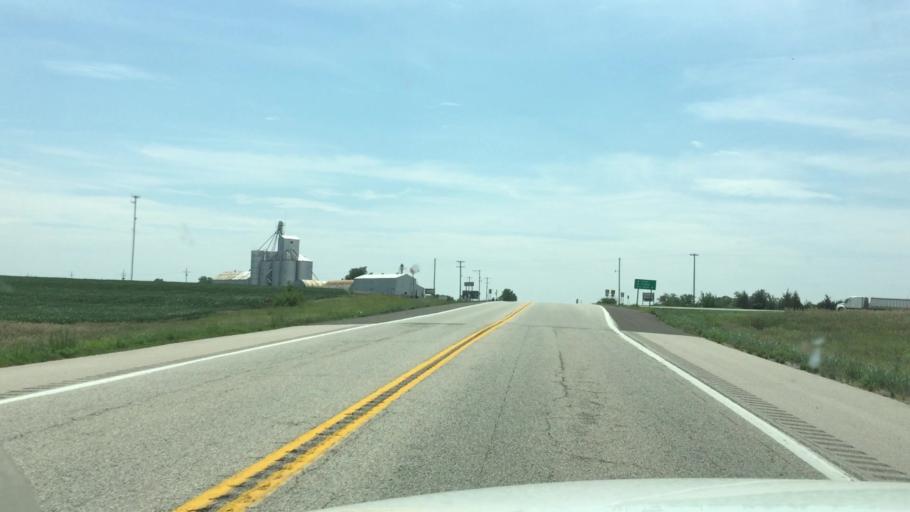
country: US
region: Kansas
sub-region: Jackson County
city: Holton
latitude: 39.6157
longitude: -95.7312
